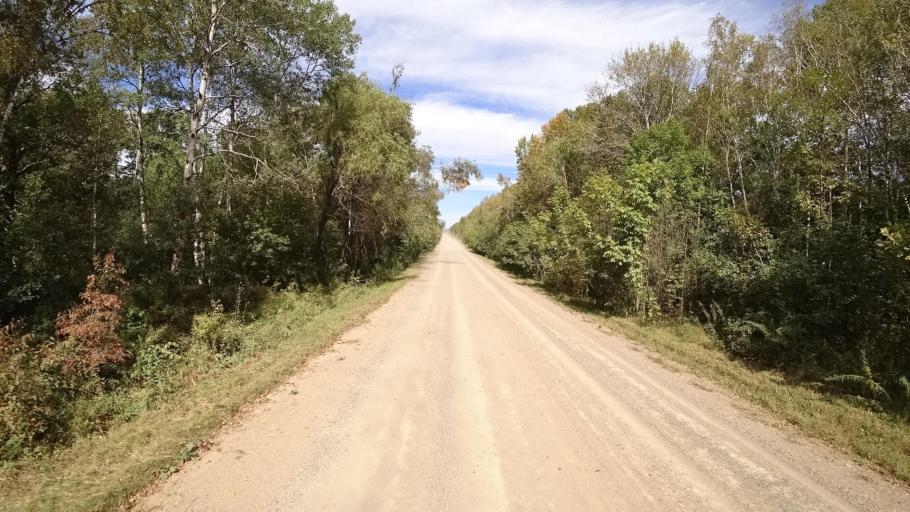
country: RU
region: Primorskiy
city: Yakovlevka
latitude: 44.6836
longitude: 133.6176
